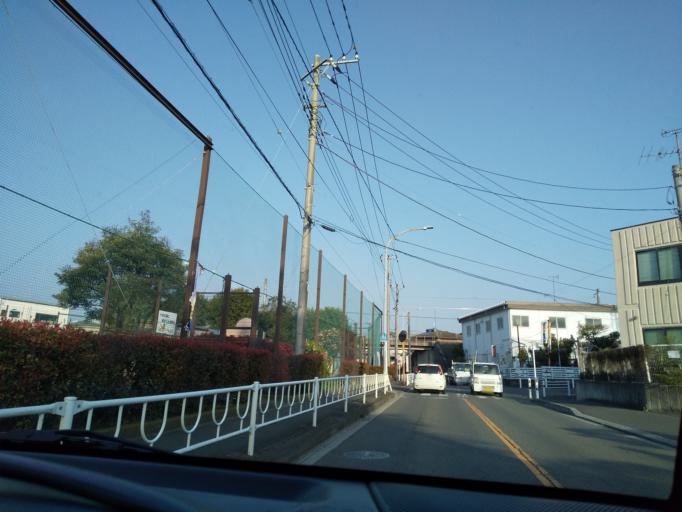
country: JP
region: Kanagawa
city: Zama
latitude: 35.5522
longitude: 139.3631
